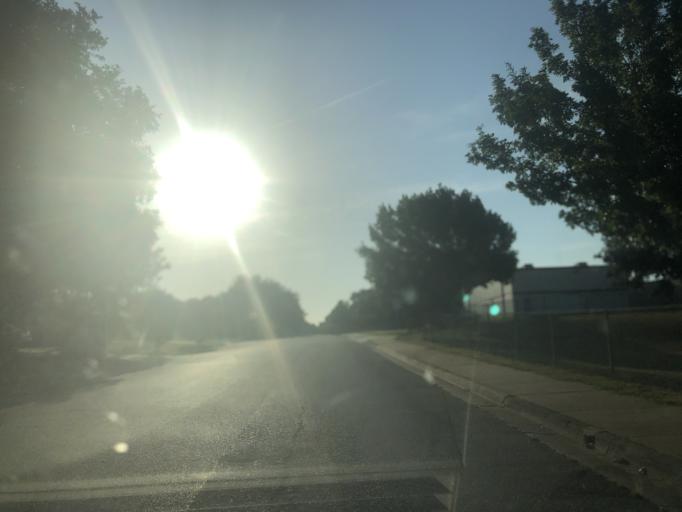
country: US
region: Texas
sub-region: Tarrant County
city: Edgecliff Village
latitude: 32.6549
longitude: -97.3943
